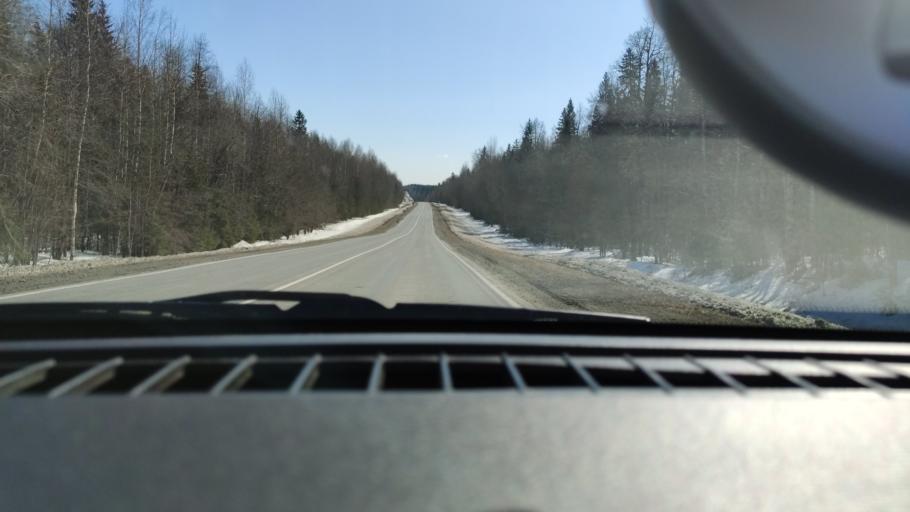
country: RU
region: Perm
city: Perm
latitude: 58.1732
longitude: 56.2323
